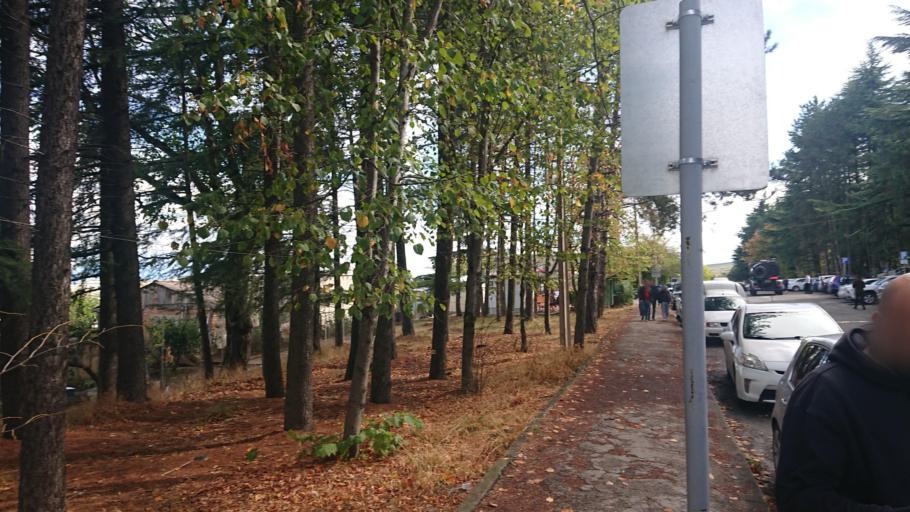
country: GE
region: Kakheti
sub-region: Telavi
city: Telavi
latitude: 41.9107
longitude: 45.4682
